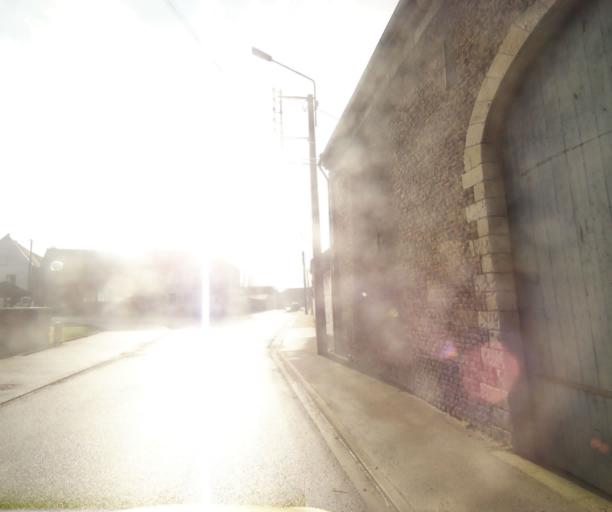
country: FR
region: Nord-Pas-de-Calais
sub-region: Departement du Nord
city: Thiant
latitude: 50.2873
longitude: 3.4556
